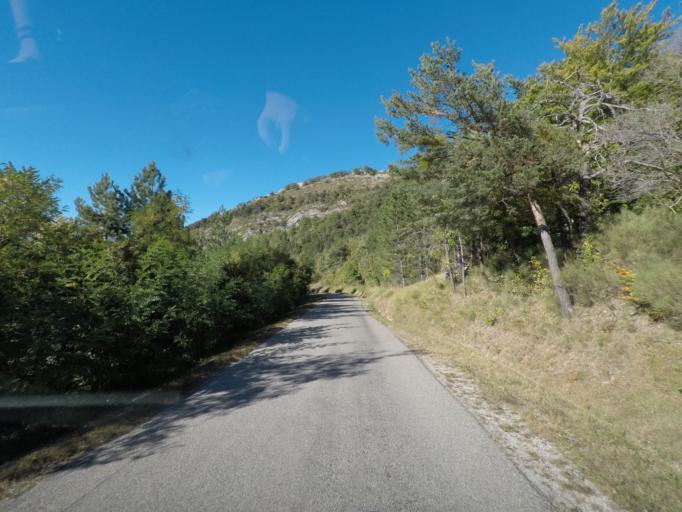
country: FR
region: Provence-Alpes-Cote d'Azur
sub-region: Departement des Hautes-Alpes
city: Serres
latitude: 44.4367
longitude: 5.5750
